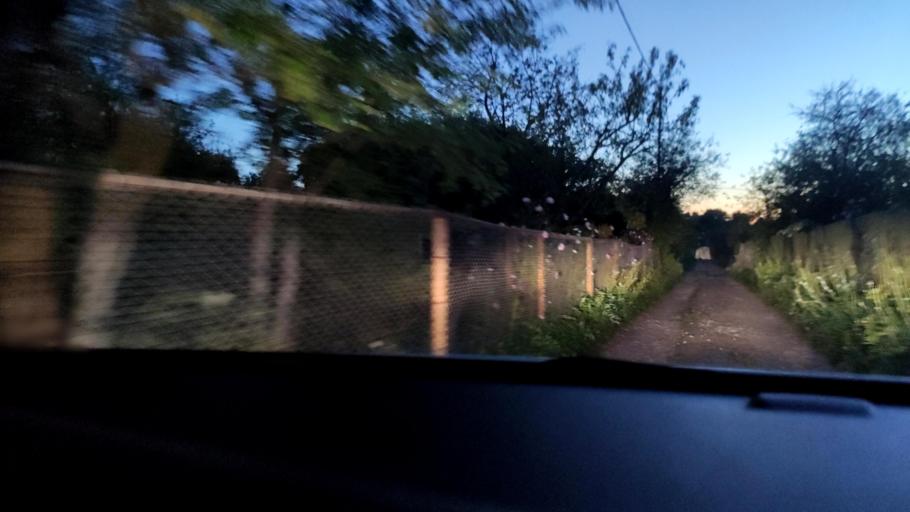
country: RU
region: Tatarstan
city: Vysokaya Gora
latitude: 55.8356
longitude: 49.2255
